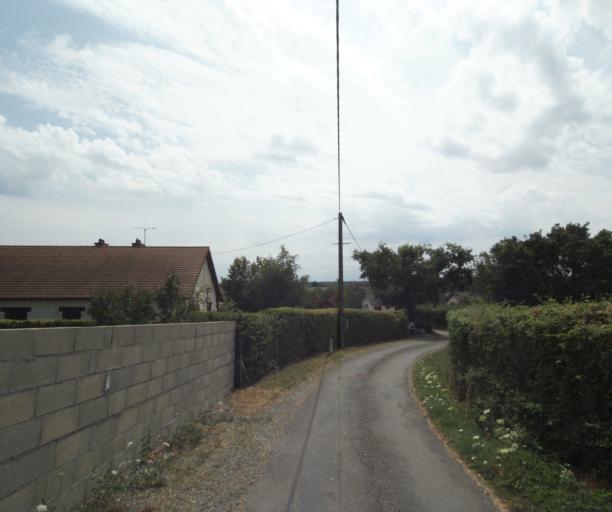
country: FR
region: Bourgogne
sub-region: Departement de Saone-et-Loire
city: Gueugnon
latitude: 46.5985
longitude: 4.0237
